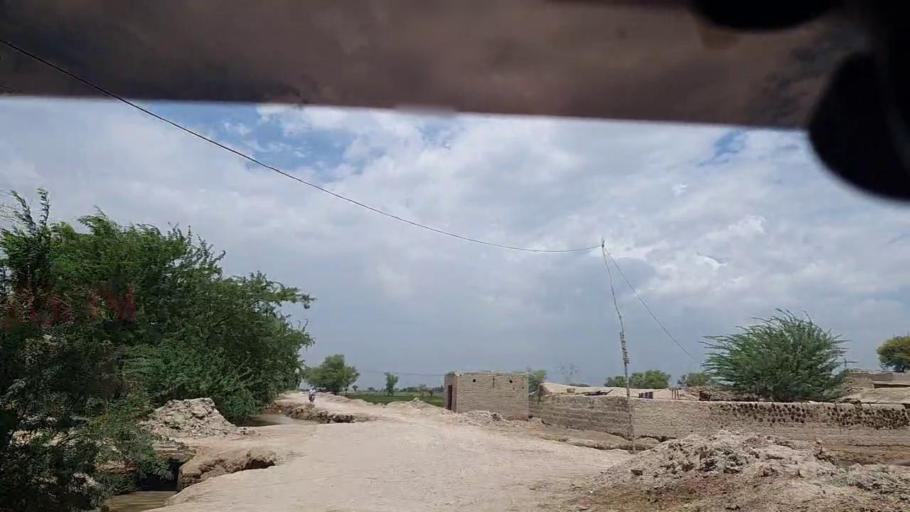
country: PK
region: Sindh
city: Ghauspur
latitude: 28.1060
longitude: 68.9861
